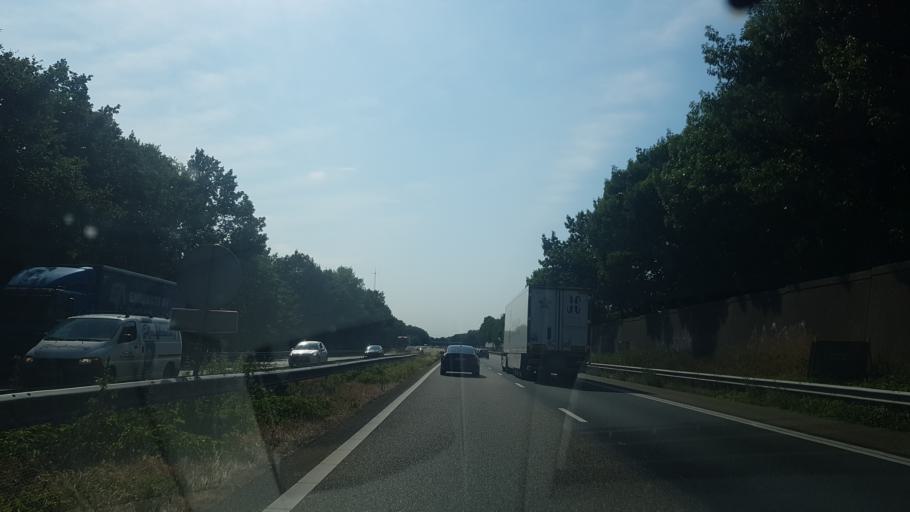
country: NL
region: North Brabant
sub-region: Roosendaal
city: Roosendaal
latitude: 51.5294
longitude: 4.4445
